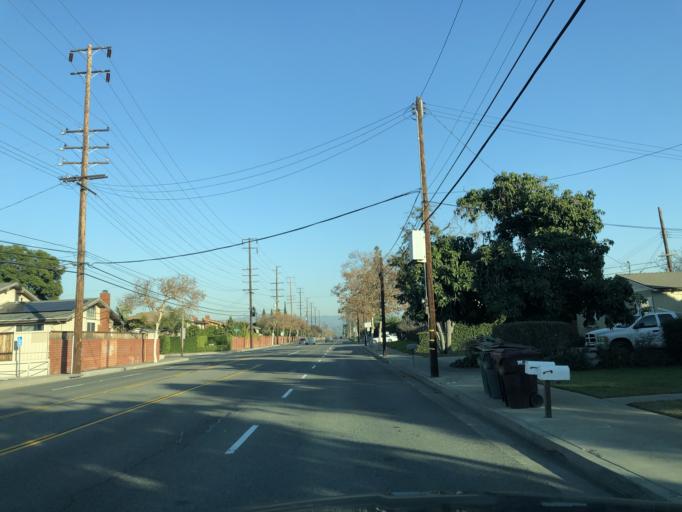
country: US
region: California
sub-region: Orange County
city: Orange
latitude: 33.7732
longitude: -117.8493
